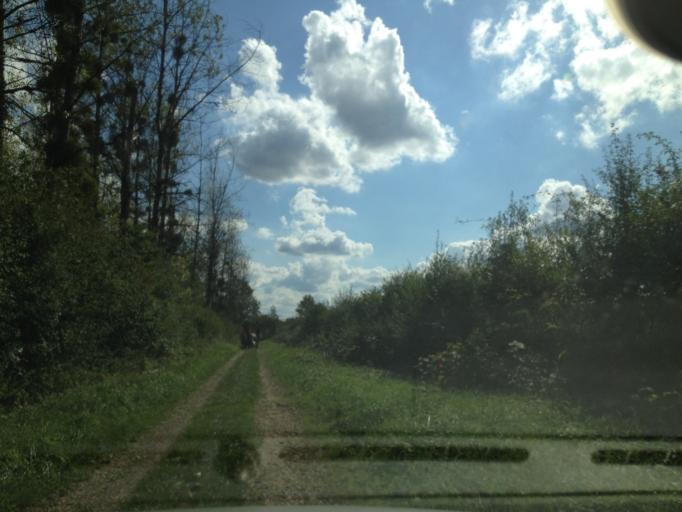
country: FR
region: Franche-Comte
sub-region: Departement de la Haute-Saone
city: Saint-Loup-sur-Semouse
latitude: 47.8267
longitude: 6.2092
